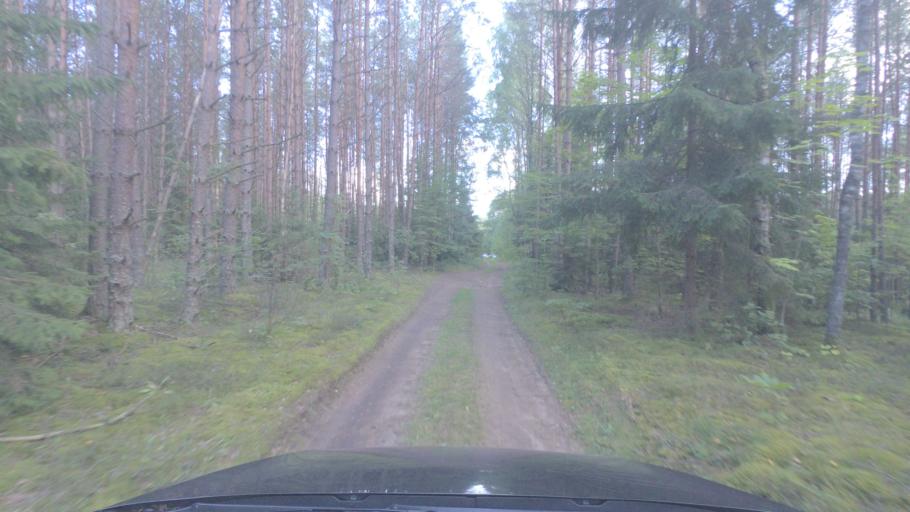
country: LT
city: Svencioneliai
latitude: 55.1604
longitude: 25.8527
